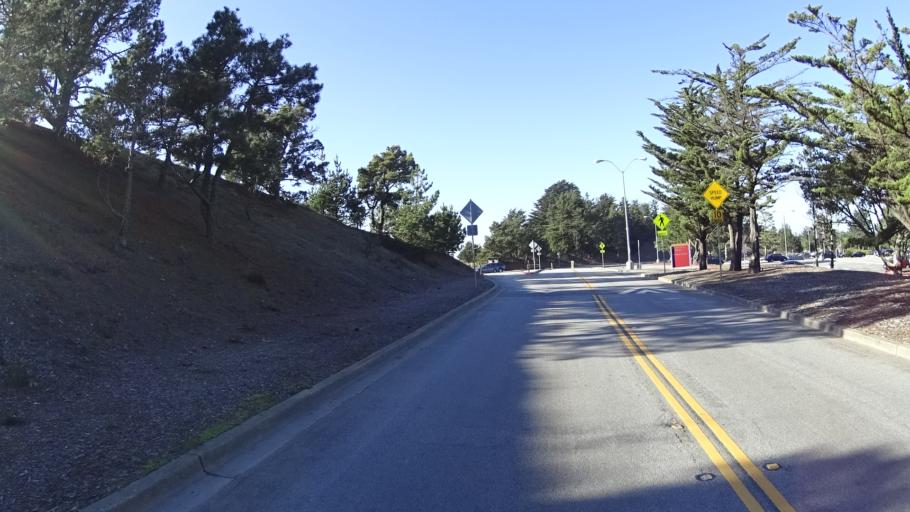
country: US
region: California
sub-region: San Mateo County
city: Pacifica
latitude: 37.6280
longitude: -122.4692
